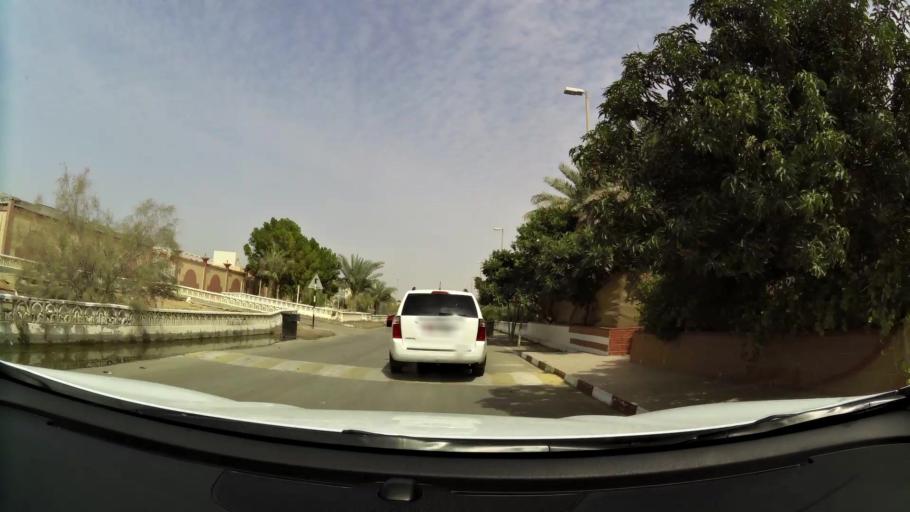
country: AE
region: Abu Dhabi
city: Abu Dhabi
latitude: 24.5241
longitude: 54.6641
